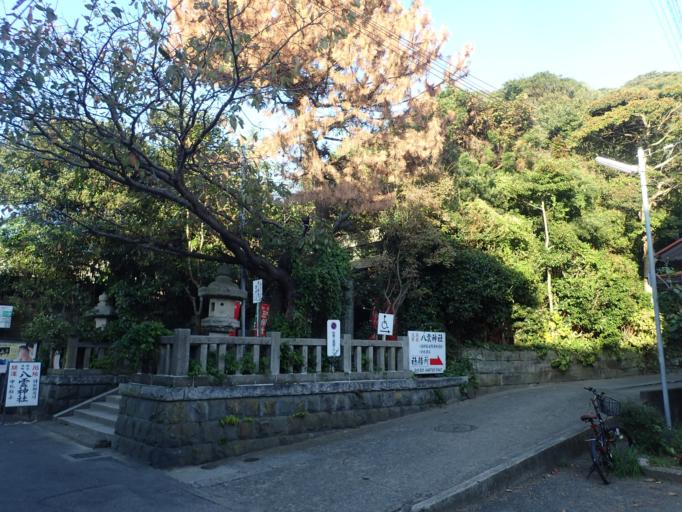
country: JP
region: Kanagawa
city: Kamakura
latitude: 35.3151
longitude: 139.5541
